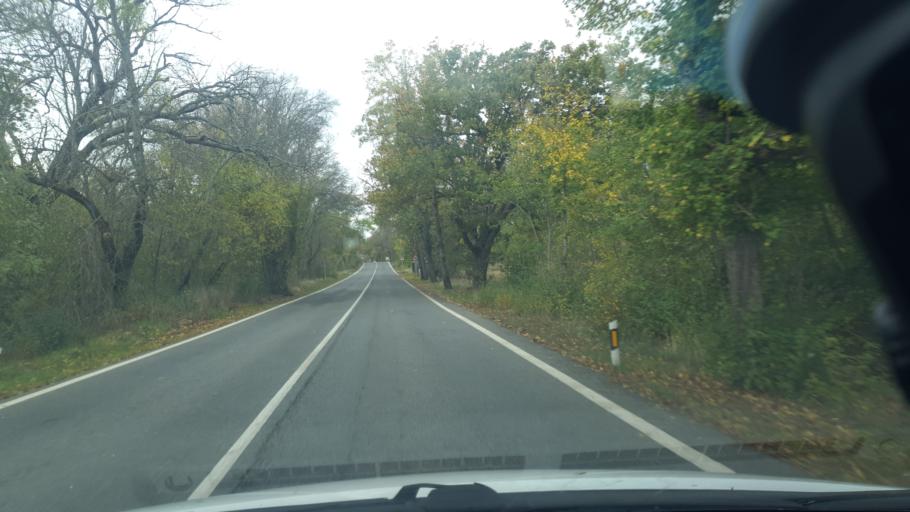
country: ES
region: Castille and Leon
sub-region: Provincia de Segovia
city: San Ildefonso
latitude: 40.9041
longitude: -4.0316
